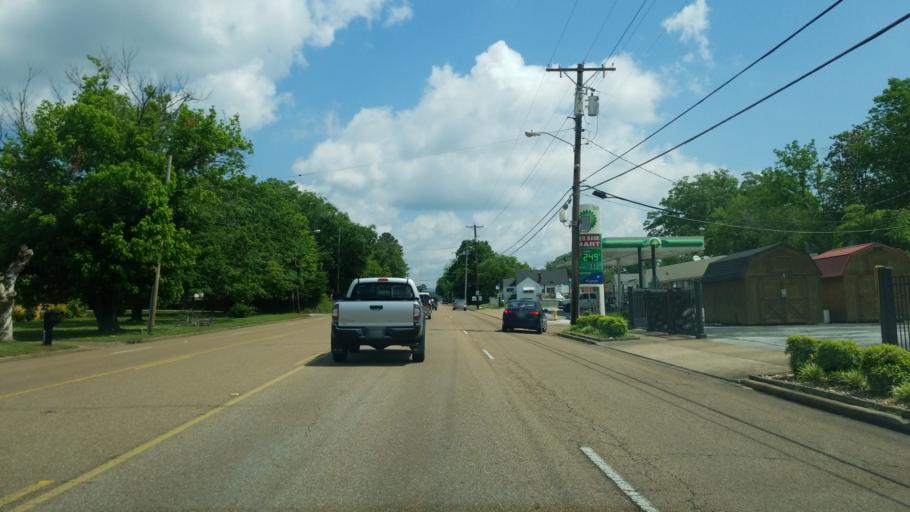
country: US
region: Tennessee
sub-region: Hamilton County
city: Red Bank
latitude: 35.1285
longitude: -85.2838
